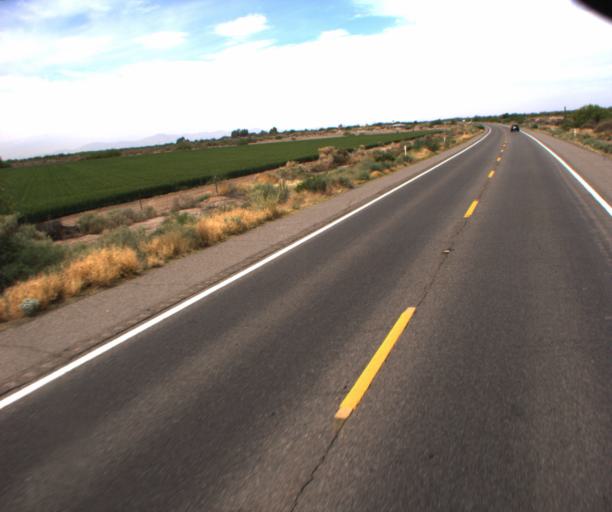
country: US
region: Arizona
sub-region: Pinal County
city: Sacaton
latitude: 33.1136
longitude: -111.7224
